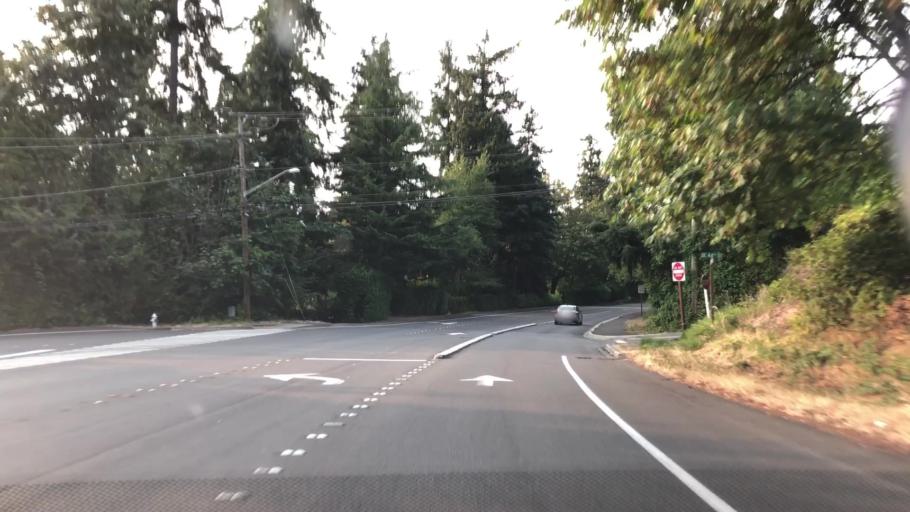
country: US
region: Washington
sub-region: King County
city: Mercer Island
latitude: 47.5671
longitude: -122.2266
